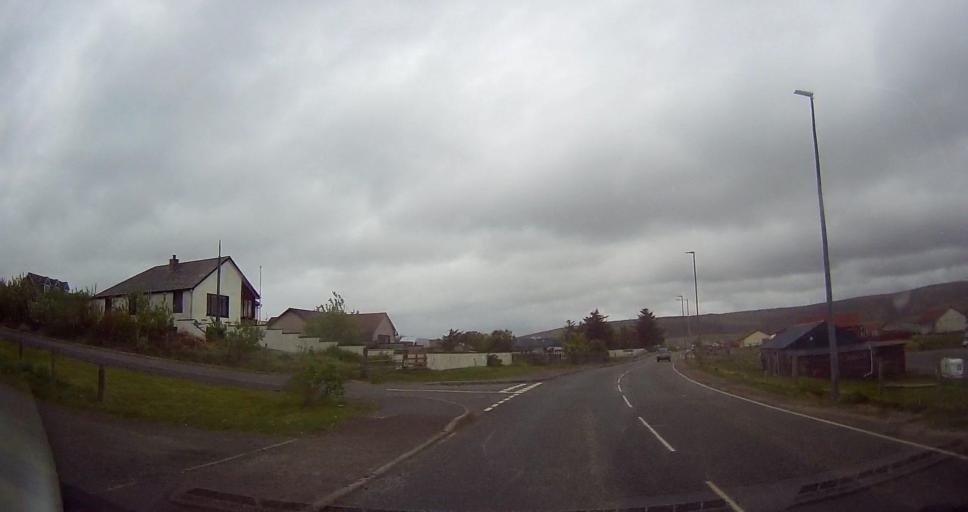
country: GB
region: Scotland
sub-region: Shetland Islands
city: Lerwick
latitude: 60.3923
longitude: -1.3670
